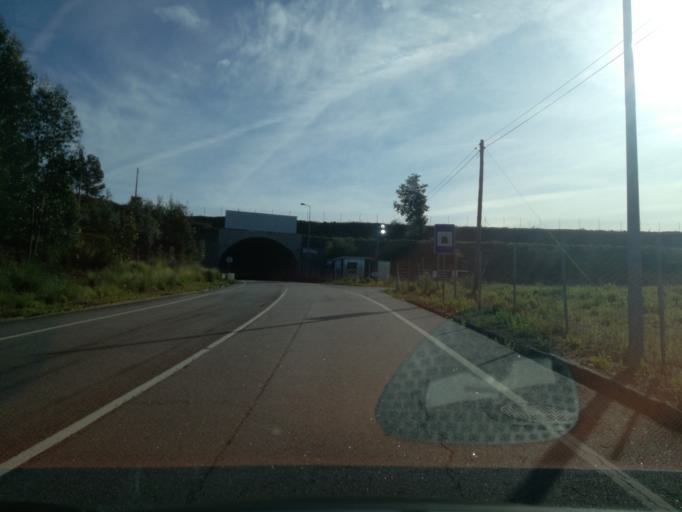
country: PT
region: Porto
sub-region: Trofa
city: Sao Romao do Coronado
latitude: 41.2814
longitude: -8.5213
